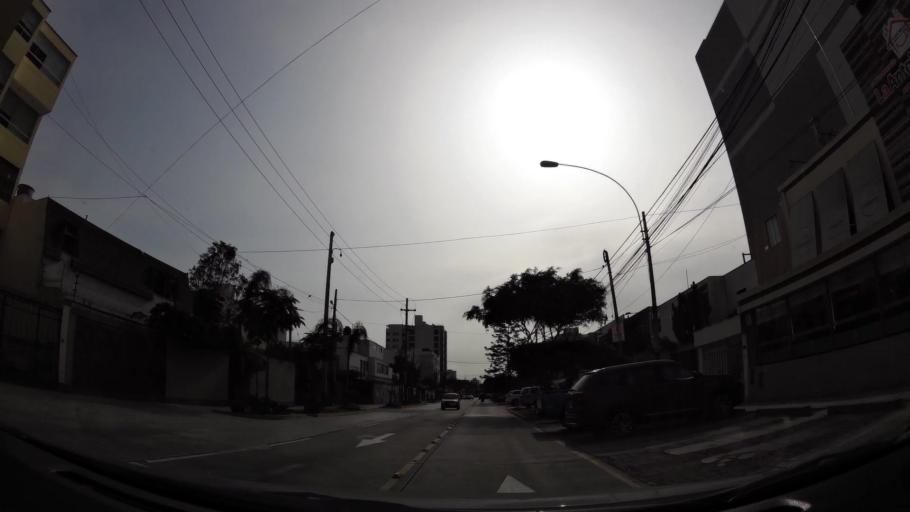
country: PE
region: Lima
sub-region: Lima
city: San Isidro
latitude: -12.0959
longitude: -77.0599
